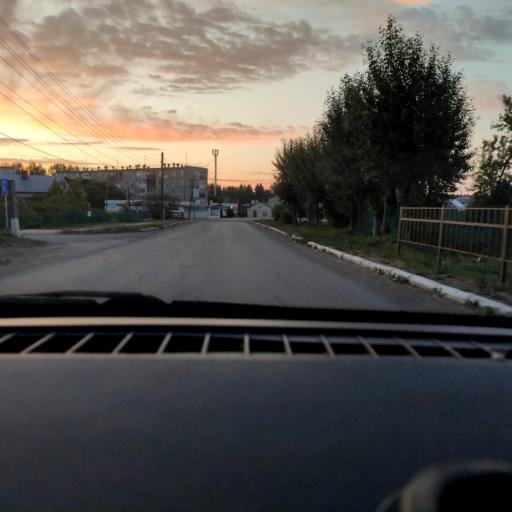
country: RU
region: Perm
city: Kukushtan
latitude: 57.6333
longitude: 56.5267
